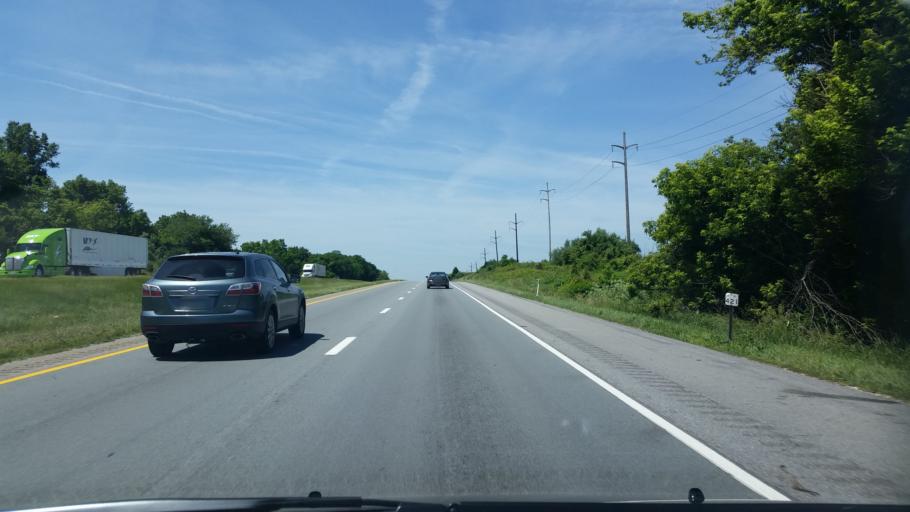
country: US
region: Pennsylvania
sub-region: Cumberland County
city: Carlisle
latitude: 40.1732
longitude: -77.2624
